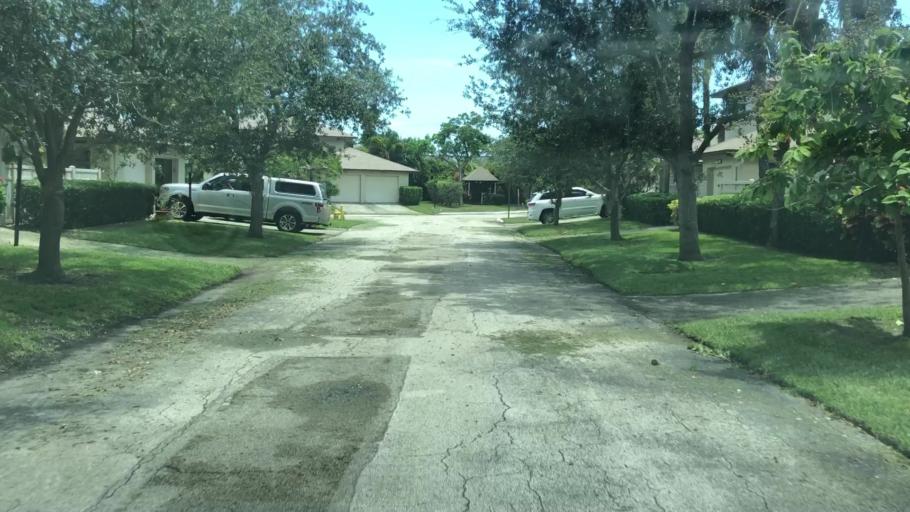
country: US
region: Florida
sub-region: Broward County
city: Pompano Beach Highlands
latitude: 26.2795
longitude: -80.0986
